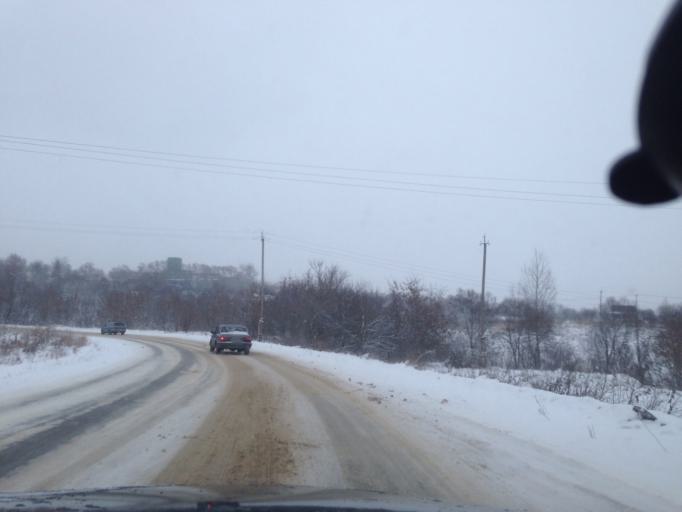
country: RU
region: Tula
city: Bolokhovo
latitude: 54.0766
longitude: 37.8212
